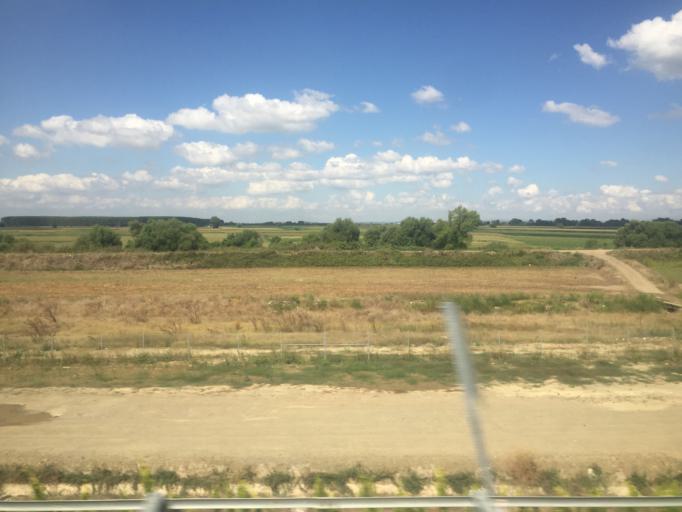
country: TR
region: Bursa
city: Tatkavakli
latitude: 40.0967
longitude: 28.2776
